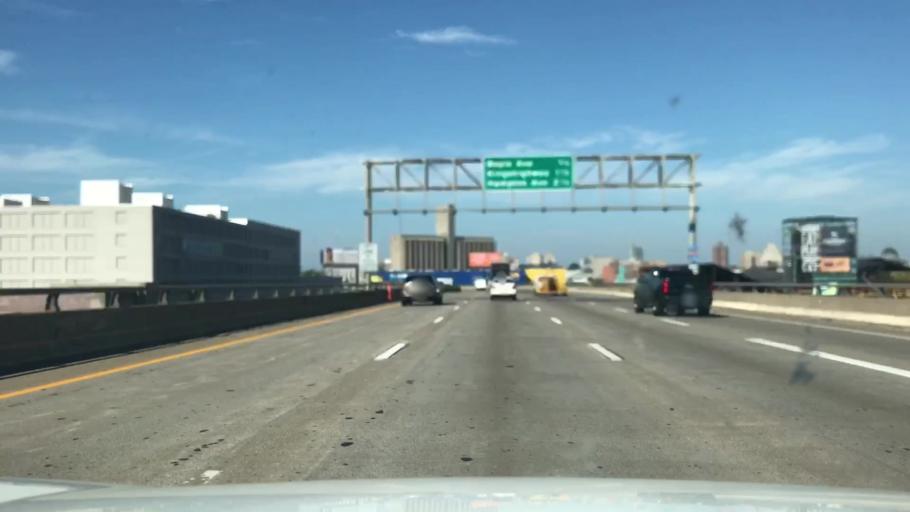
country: US
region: Missouri
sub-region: City of Saint Louis
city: St. Louis
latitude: 38.6321
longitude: -90.2377
